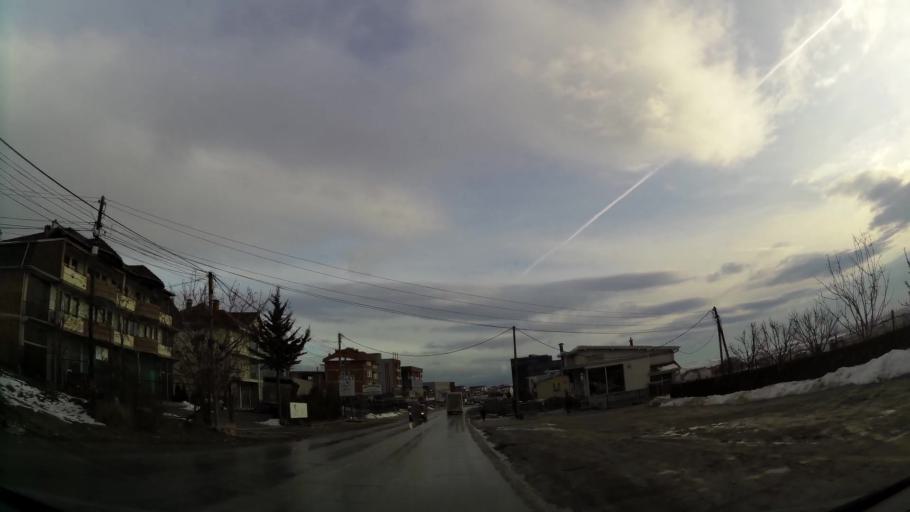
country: XK
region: Pristina
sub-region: Komuna e Prishtines
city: Pristina
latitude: 42.6284
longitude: 21.1601
